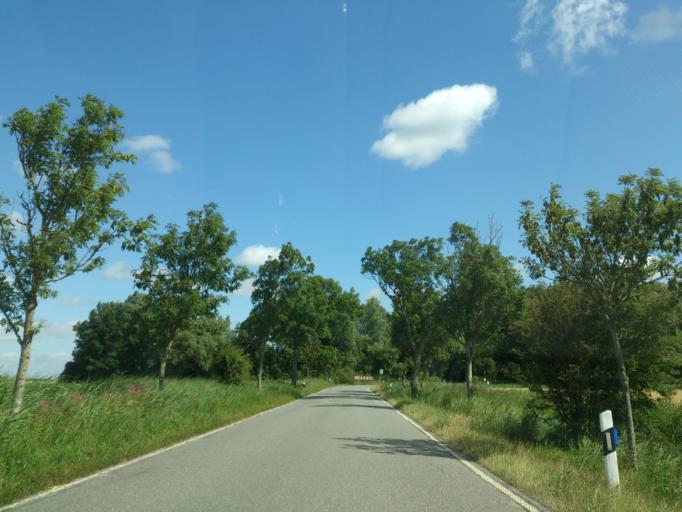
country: DE
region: Schleswig-Holstein
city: Katharinenheerd
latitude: 54.3151
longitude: 8.8393
